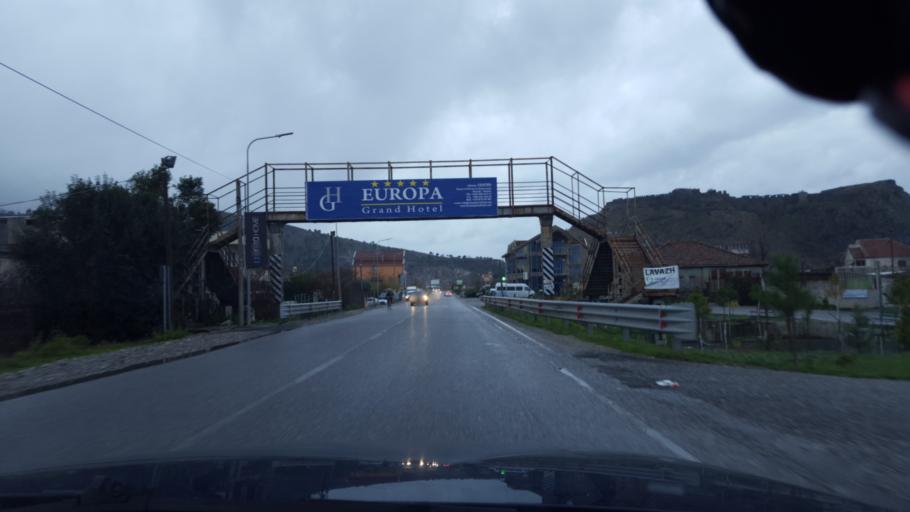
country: AL
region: Shkoder
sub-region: Rrethi i Shkodres
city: Berdica e Madhe
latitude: 42.0386
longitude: 19.4969
